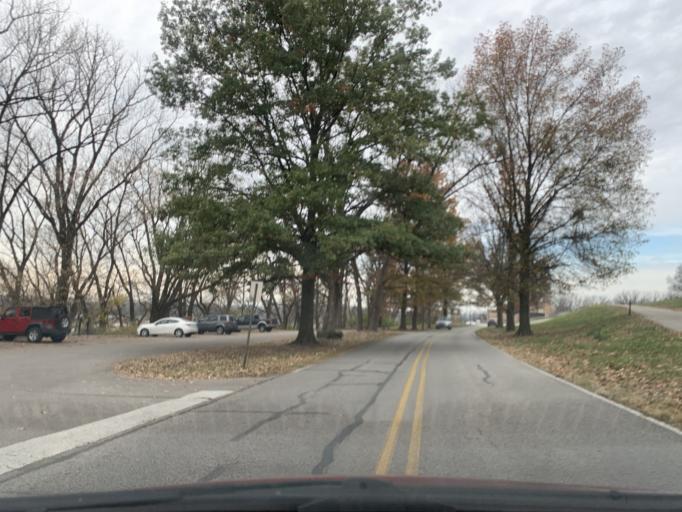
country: US
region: Kentucky
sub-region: Jefferson County
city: Louisville
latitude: 38.2745
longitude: -85.7612
